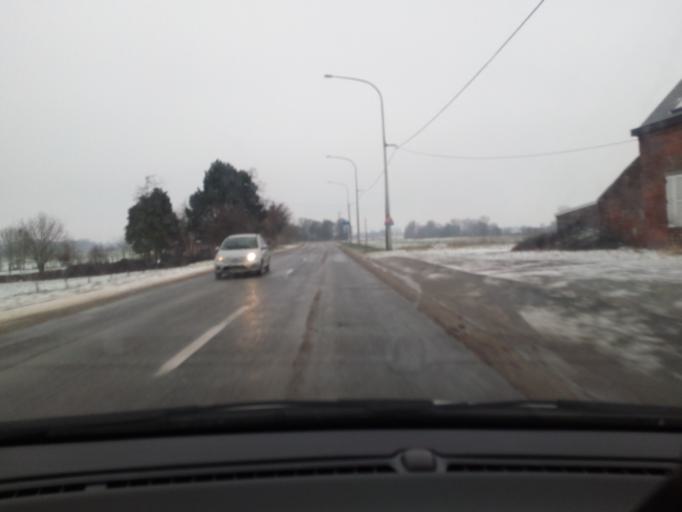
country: FR
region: Nord-Pas-de-Calais
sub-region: Departement du Nord
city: La Longueville
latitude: 50.3413
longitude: 3.8767
